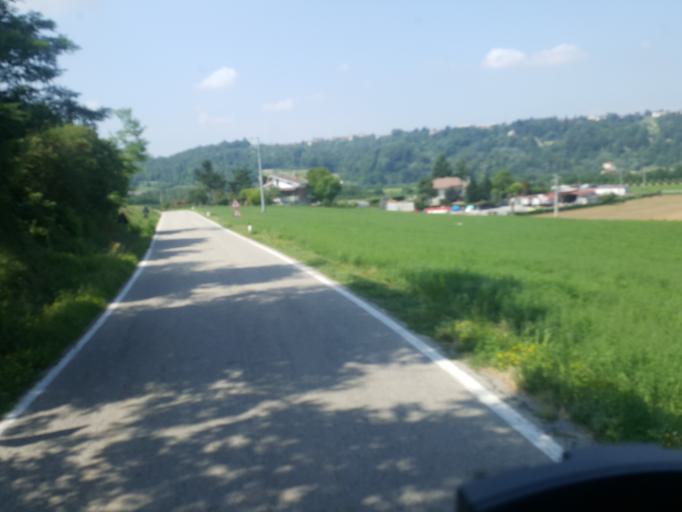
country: IT
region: Piedmont
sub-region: Provincia di Cuneo
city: Narzole
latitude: 44.6061
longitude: 7.8924
